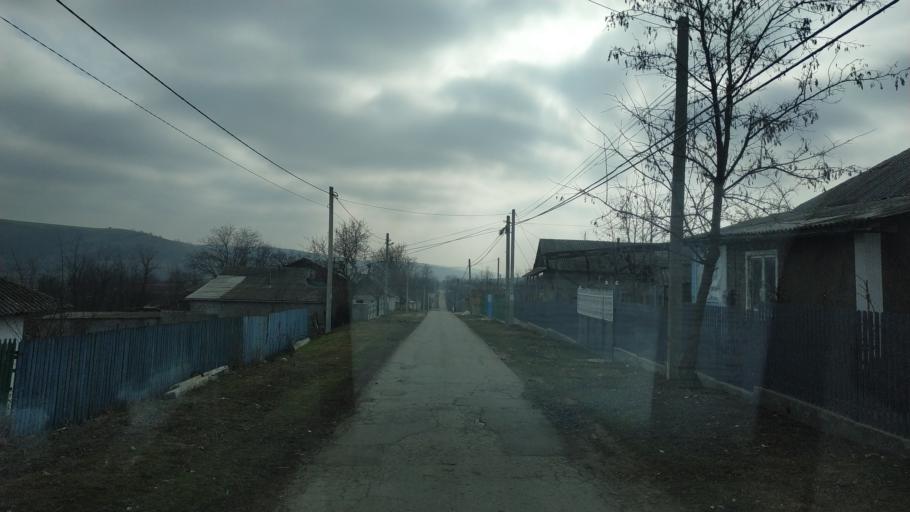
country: MD
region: Hincesti
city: Dancu
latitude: 46.8851
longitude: 28.3214
